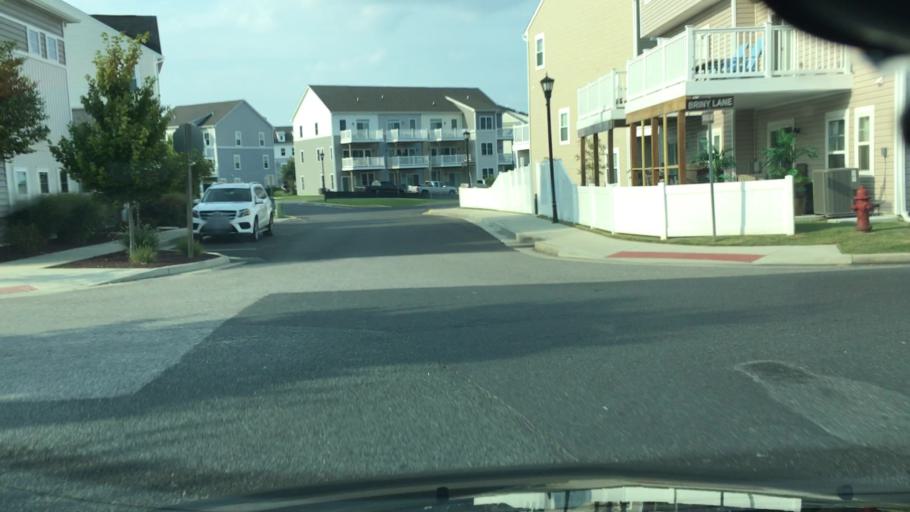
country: US
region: Maryland
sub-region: Worcester County
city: West Ocean City
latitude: 38.3364
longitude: -75.1033
